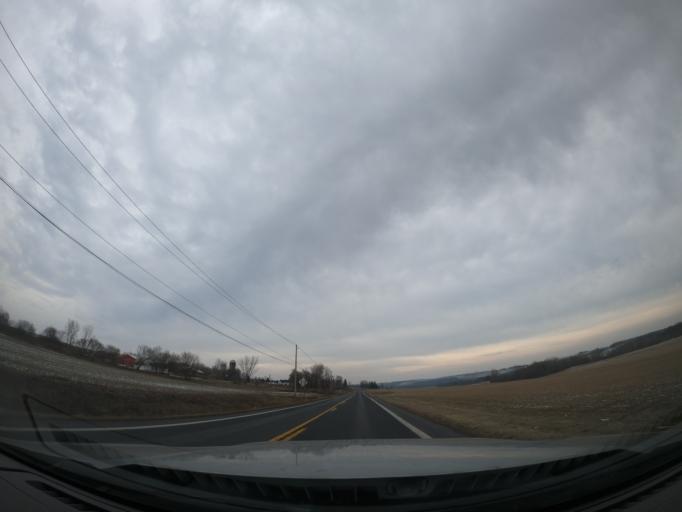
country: US
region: New York
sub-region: Cayuga County
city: Moravia
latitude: 42.7619
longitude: -76.5571
